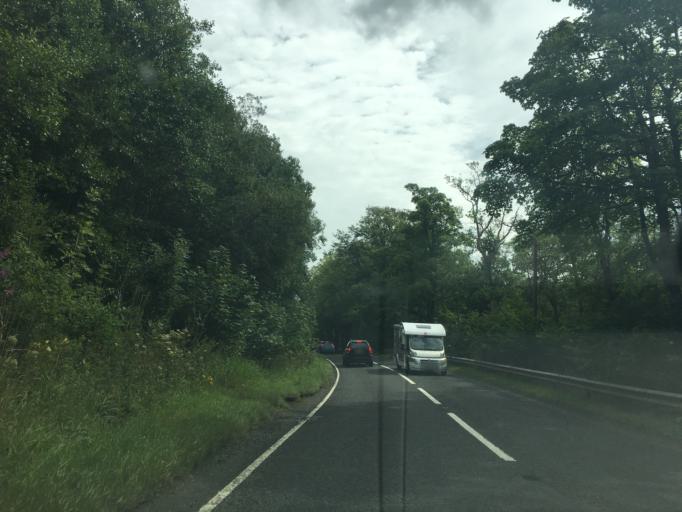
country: GB
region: Scotland
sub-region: Stirling
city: Callander
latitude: 56.2505
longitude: -4.2602
